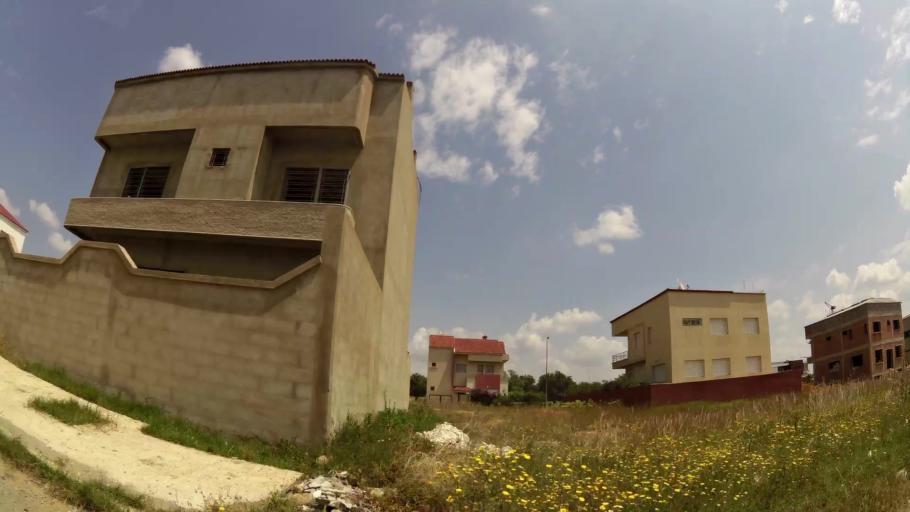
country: MA
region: Gharb-Chrarda-Beni Hssen
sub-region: Kenitra Province
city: Kenitra
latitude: 34.0138
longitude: -6.5366
